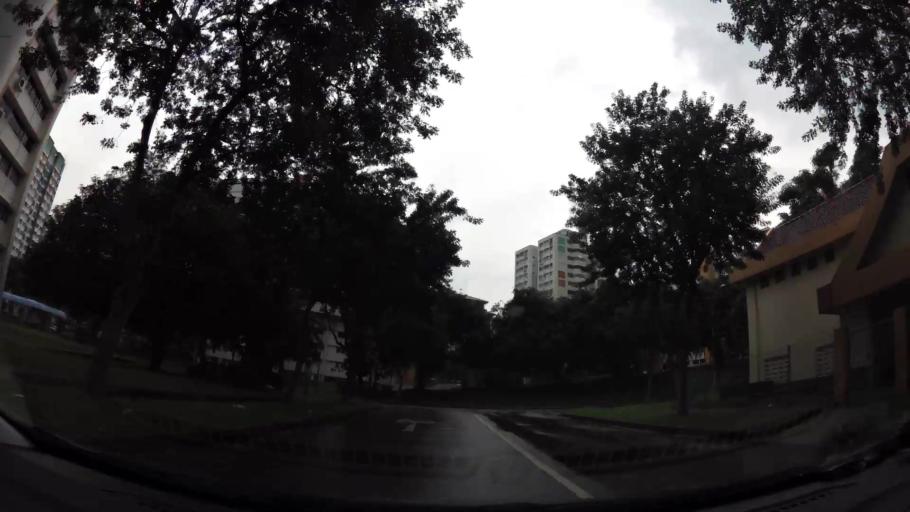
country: SG
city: Singapore
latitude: 1.3353
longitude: 103.8810
